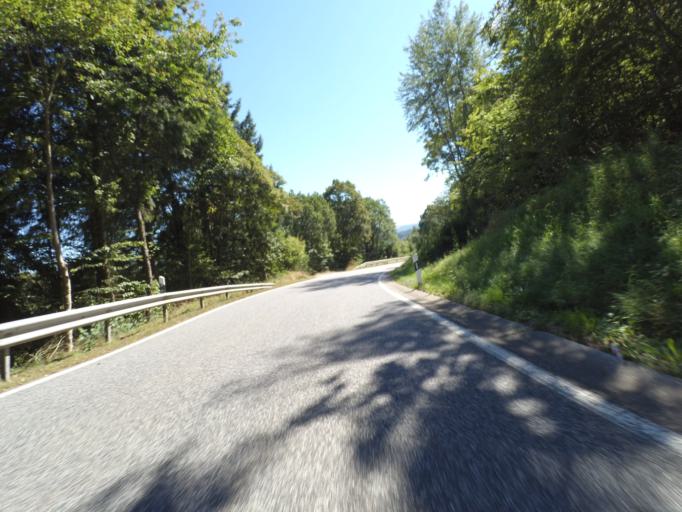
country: DE
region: Rheinland-Pfalz
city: Bremm
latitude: 50.0984
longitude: 7.1086
